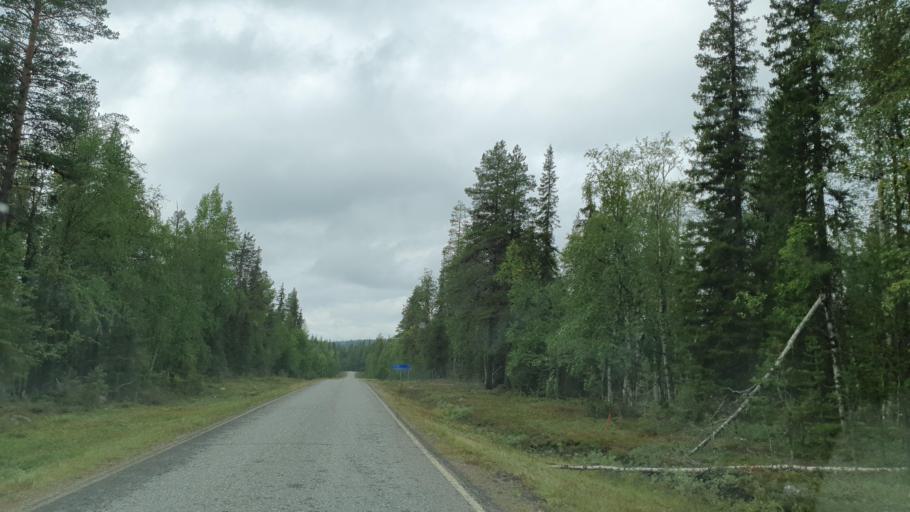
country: FI
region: Lapland
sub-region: Tunturi-Lappi
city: Kittilae
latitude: 67.7402
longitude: 24.3004
